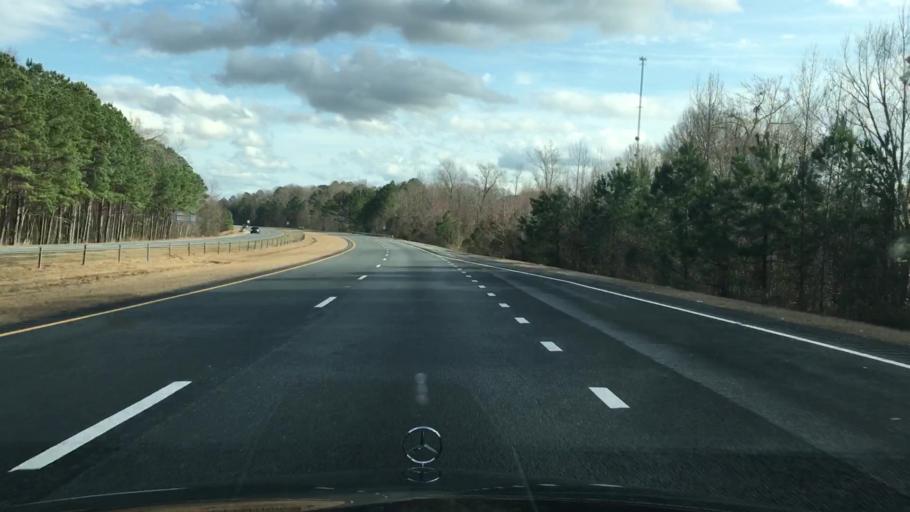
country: US
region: North Carolina
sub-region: Johnston County
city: Four Oaks
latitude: 35.3274
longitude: -78.4424
